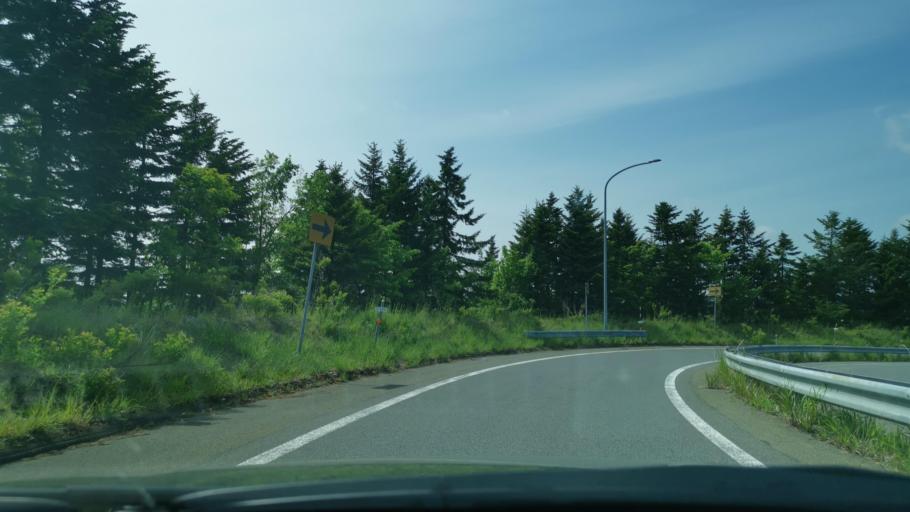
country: JP
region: Hokkaido
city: Iwamizawa
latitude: 43.1783
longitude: 141.7617
